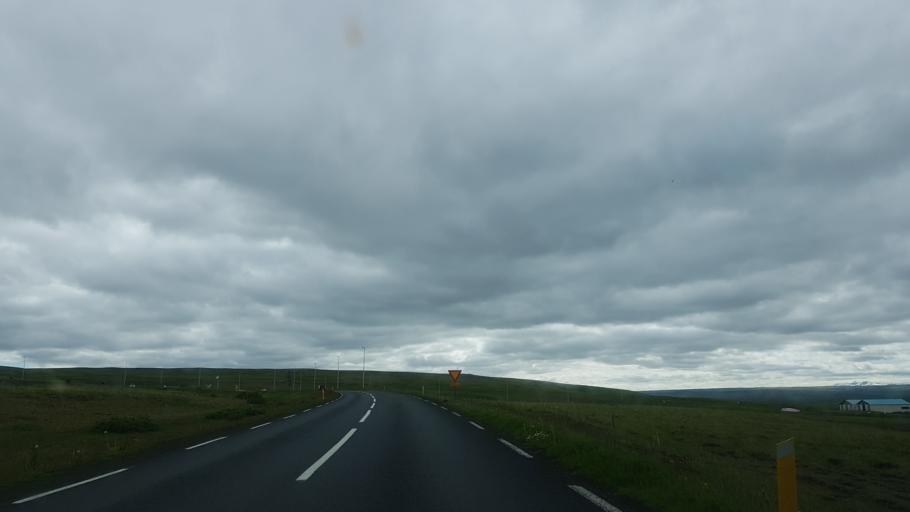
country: IS
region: Northwest
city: Saudarkrokur
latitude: 65.3554
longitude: -20.8882
